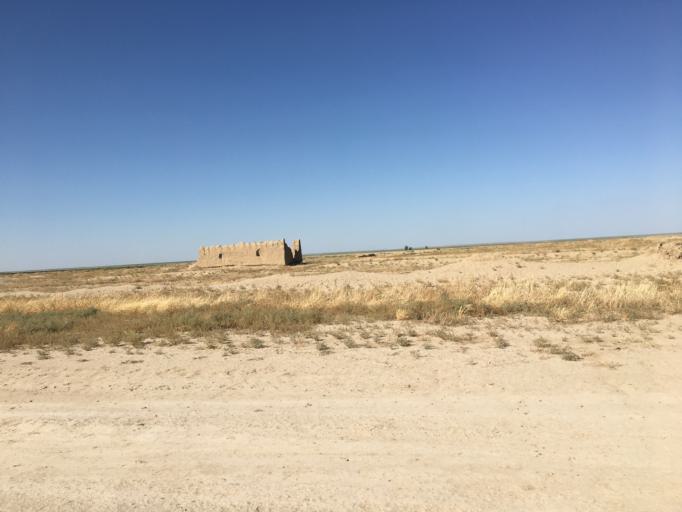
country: TM
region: Ahal
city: Tejen
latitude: 36.9797
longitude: 60.2513
